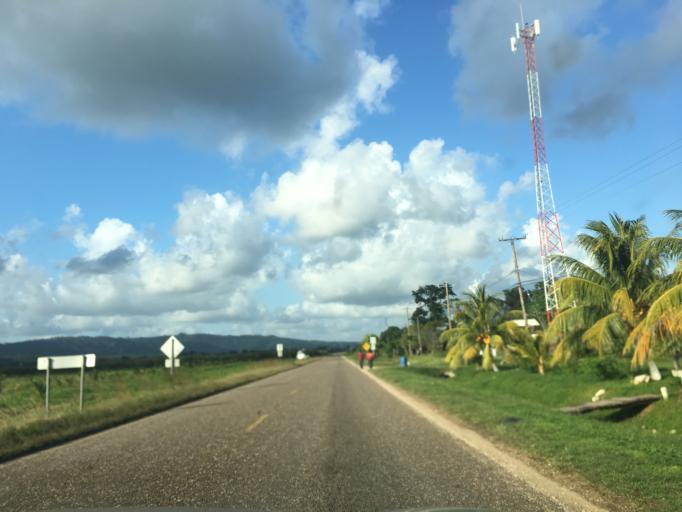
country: BZ
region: Stann Creek
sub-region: Dangriga
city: Dangriga
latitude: 16.8003
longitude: -88.3799
